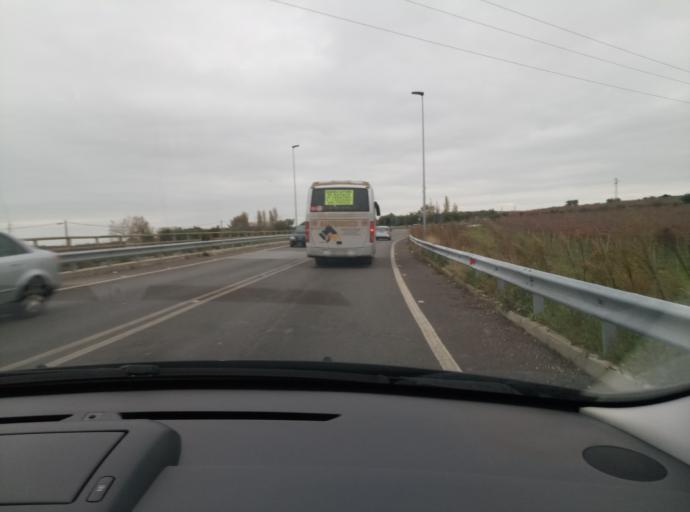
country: IT
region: Apulia
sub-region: Provincia di Bari
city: Acquaviva delle Fonti
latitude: 40.8833
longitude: 16.8128
